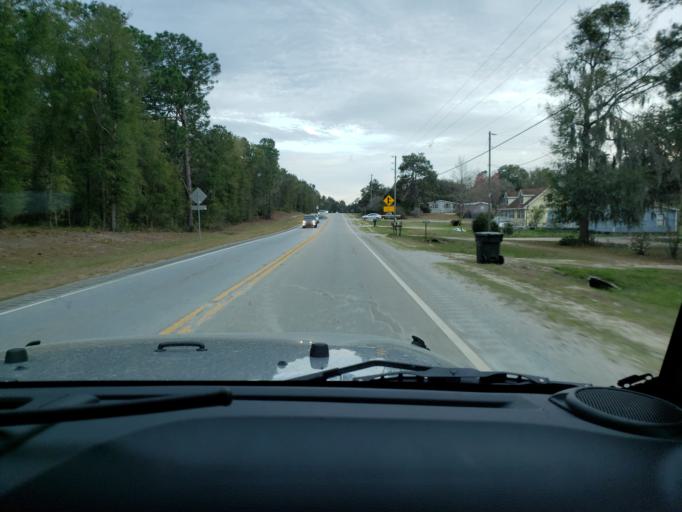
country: US
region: Georgia
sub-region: Bryan County
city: Richmond Hill
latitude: 32.0300
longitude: -81.3225
